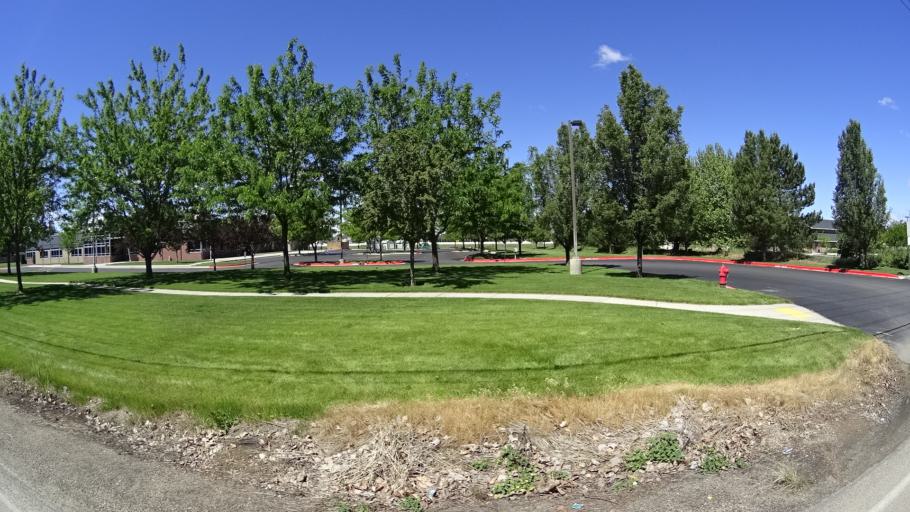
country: US
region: Idaho
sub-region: Ada County
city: Eagle
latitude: 43.6605
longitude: -116.3746
